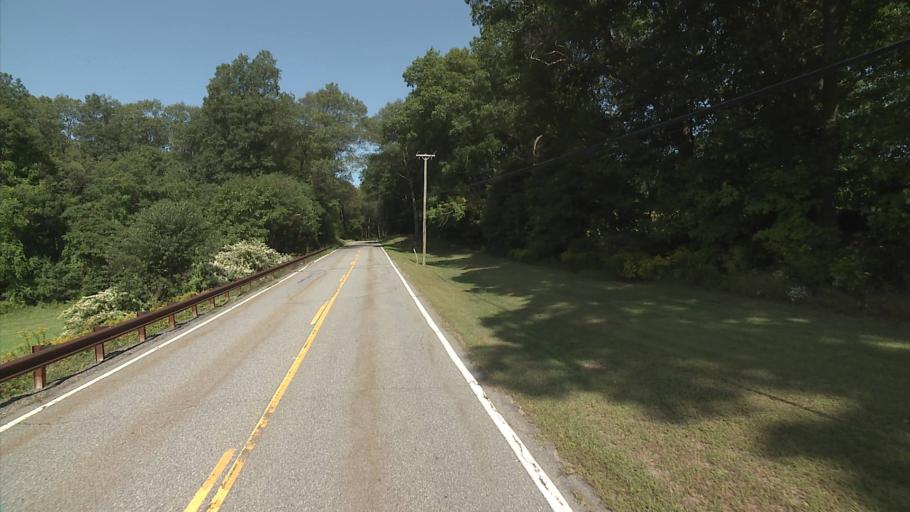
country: US
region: Connecticut
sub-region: Windham County
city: Quinebaug
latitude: 42.0187
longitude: -72.0075
